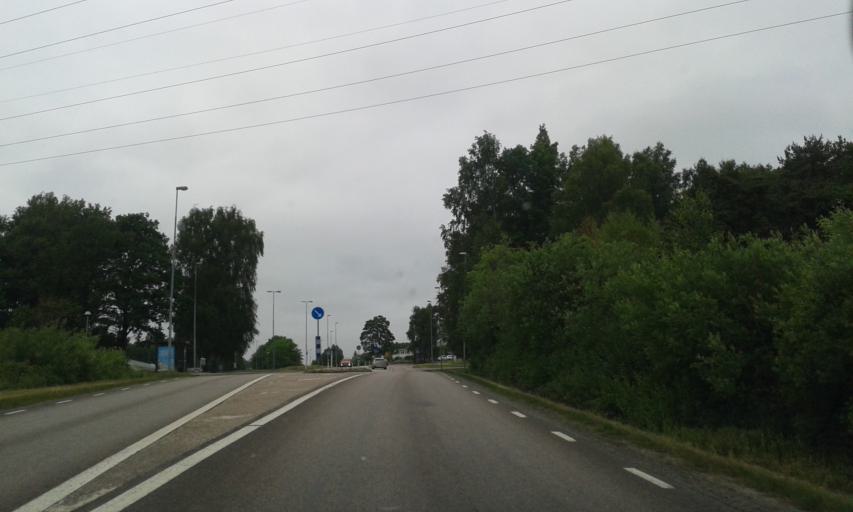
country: SE
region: Vaestra Goetaland
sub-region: Kungalvs Kommun
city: Kungalv
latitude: 57.8813
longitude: 11.9716
